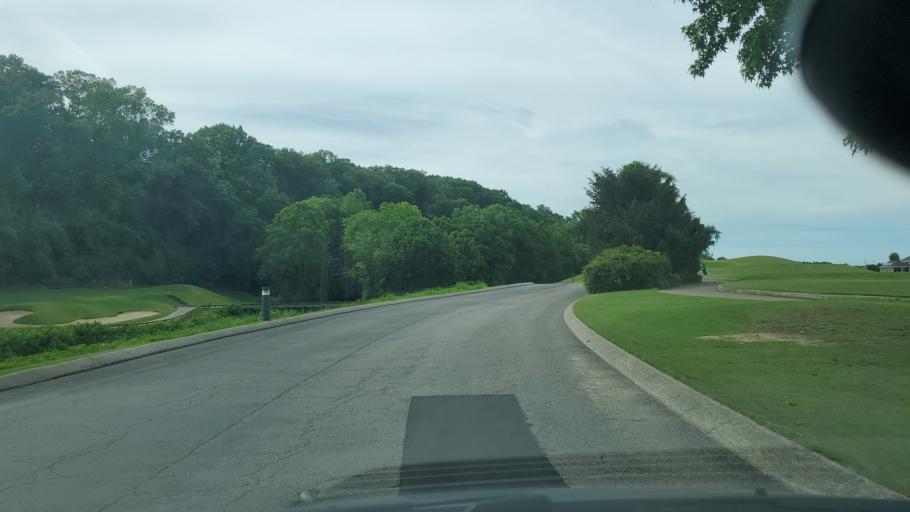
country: US
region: Tennessee
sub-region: Davidson County
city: Lakewood
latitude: 36.2156
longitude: -86.6812
